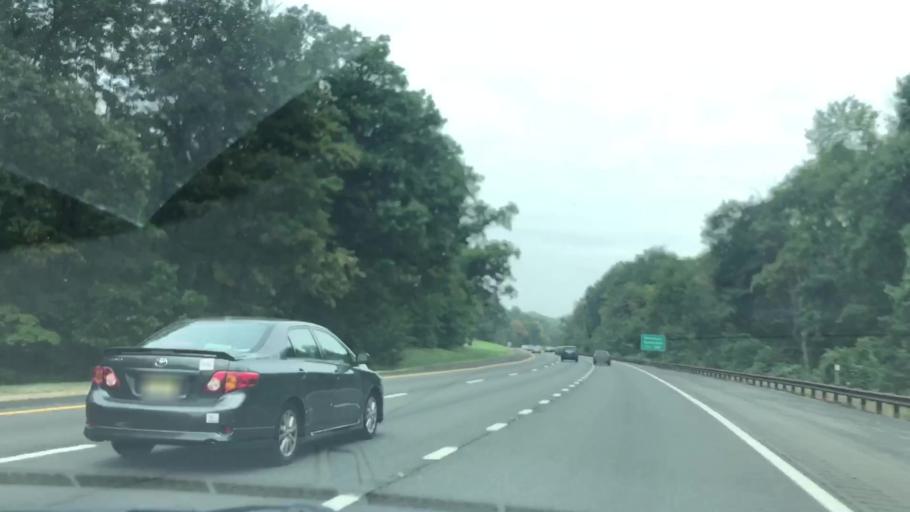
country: US
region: New Jersey
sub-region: Bergen County
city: Ho-Ho-Kus
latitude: 40.9841
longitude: -74.0710
